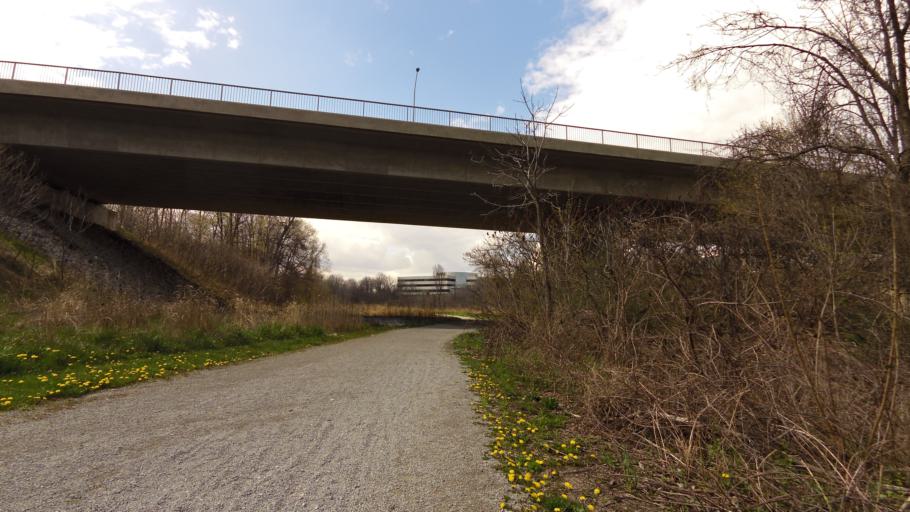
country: CA
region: Ontario
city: Etobicoke
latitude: 43.6509
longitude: -79.6177
